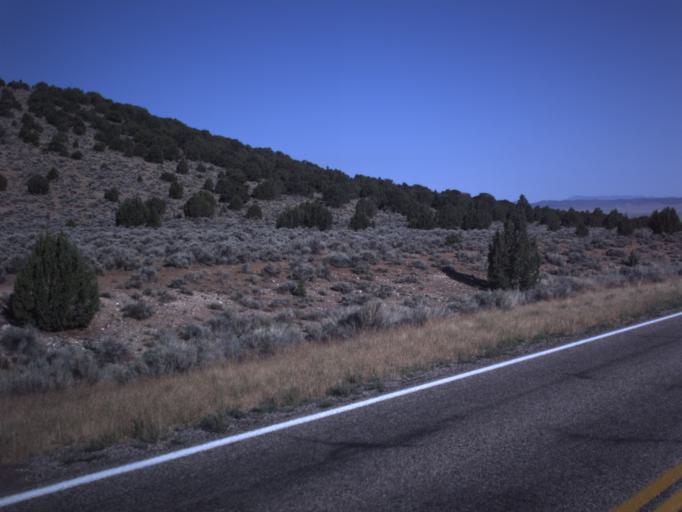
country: US
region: Utah
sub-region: Beaver County
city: Milford
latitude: 38.1289
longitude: -112.9582
